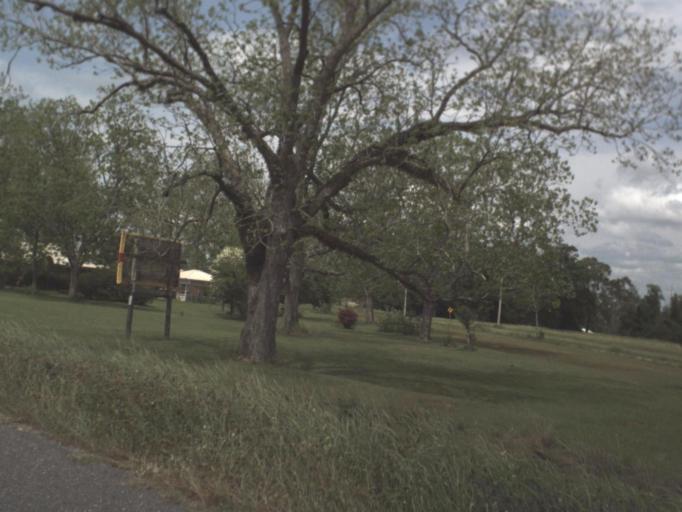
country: US
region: Alabama
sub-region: Escambia County
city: East Brewton
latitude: 30.9887
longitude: -87.1142
